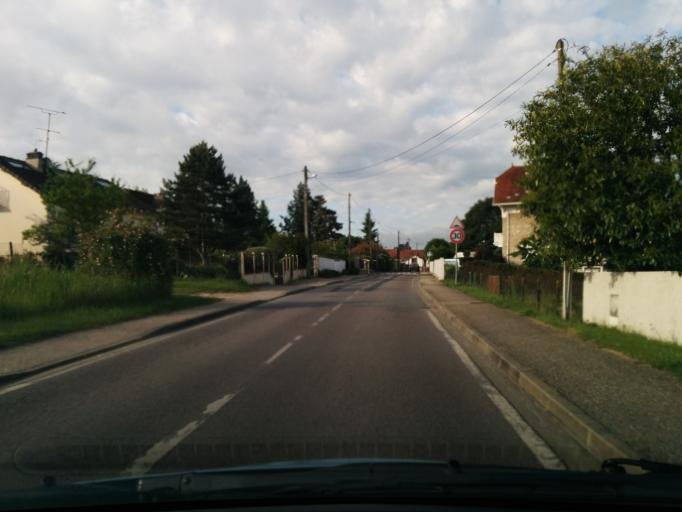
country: FR
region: Ile-de-France
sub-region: Departement des Yvelines
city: Follainville-Dennemont
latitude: 49.0438
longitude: 1.6894
